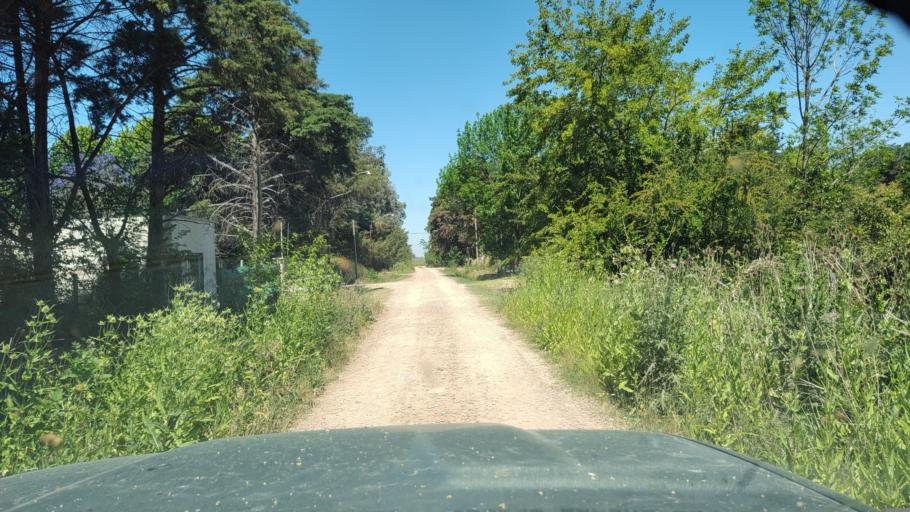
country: AR
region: Buenos Aires
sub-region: Partido de Lujan
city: Lujan
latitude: -34.5988
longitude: -59.1406
